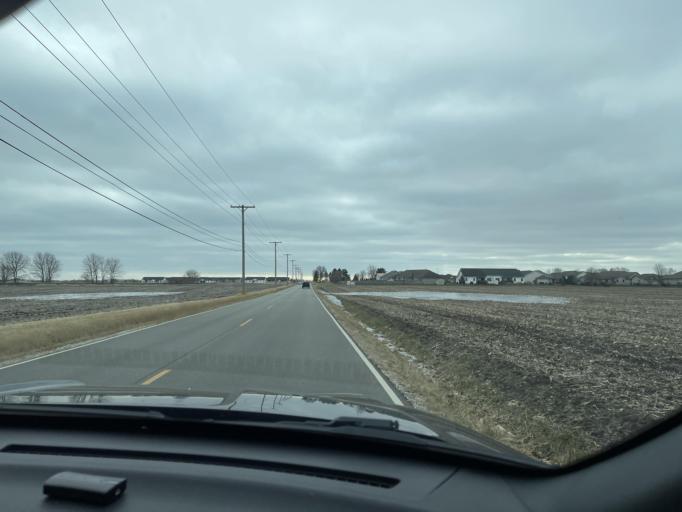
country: US
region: Illinois
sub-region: Sangamon County
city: Jerome
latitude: 39.7683
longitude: -89.7534
